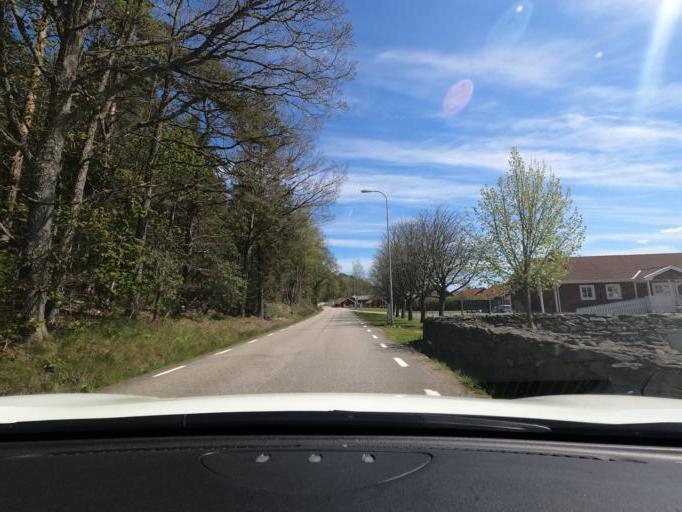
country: SE
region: Vaestra Goetaland
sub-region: Marks Kommun
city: Horred
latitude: 57.4244
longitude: 12.3322
